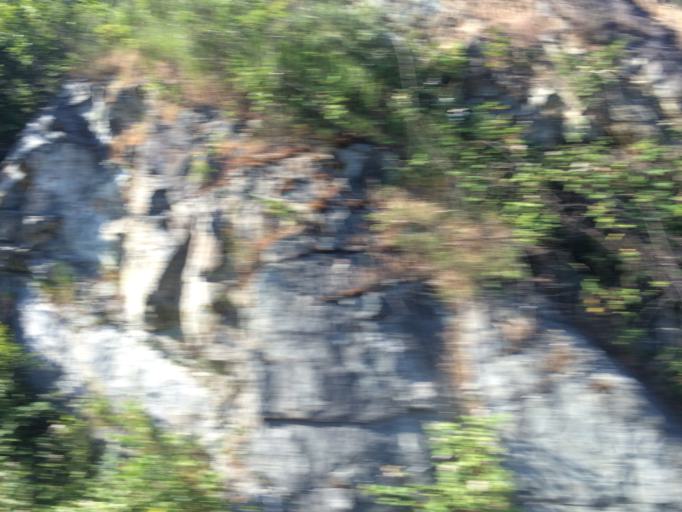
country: CA
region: British Columbia
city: Victoria
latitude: 48.4639
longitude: -123.4205
